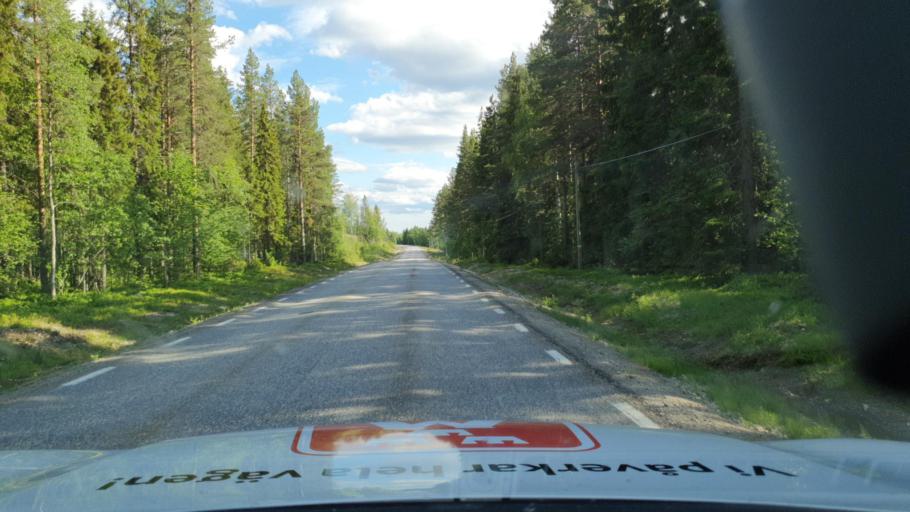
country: SE
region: Vaesterbotten
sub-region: Skelleftea Kommun
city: Langsele
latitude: 64.7342
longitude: 19.9534
